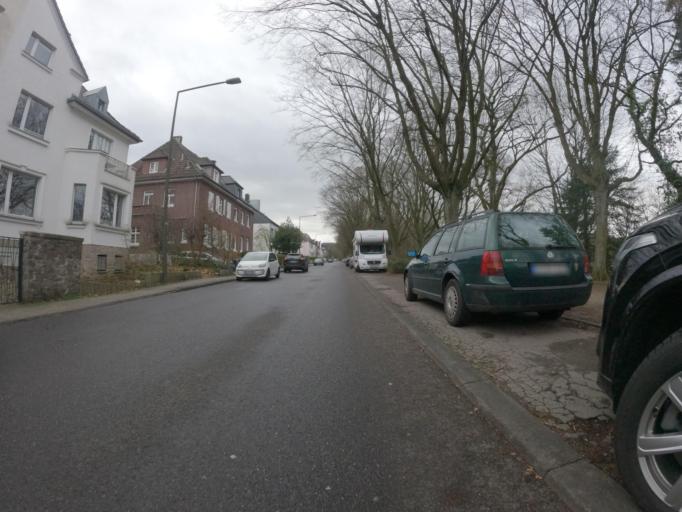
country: DE
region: North Rhine-Westphalia
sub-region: Regierungsbezirk Koln
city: Aachen
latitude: 50.7546
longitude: 6.0750
